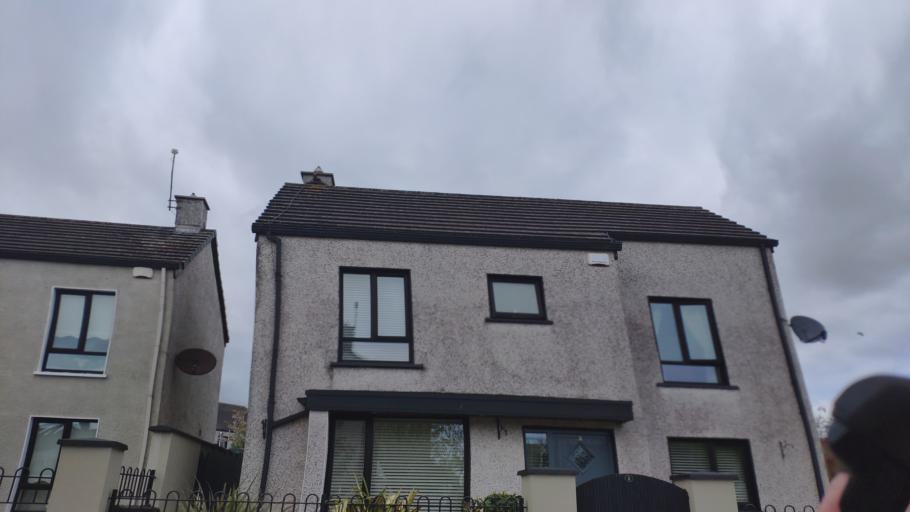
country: IE
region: Munster
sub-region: County Cork
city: Cork
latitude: 51.9107
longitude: -8.5048
